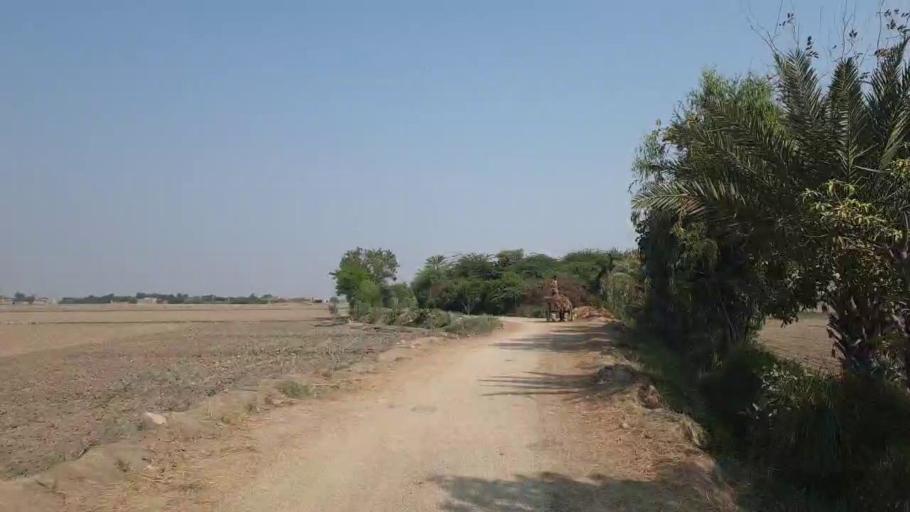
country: PK
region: Sindh
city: Matli
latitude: 24.9766
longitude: 68.5889
